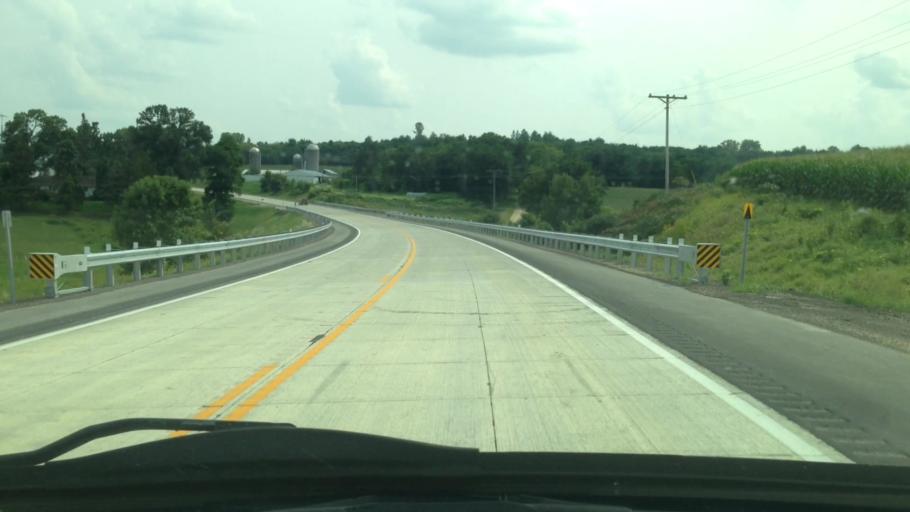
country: US
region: Minnesota
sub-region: Olmsted County
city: Oronoco
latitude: 44.1501
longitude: -92.4194
